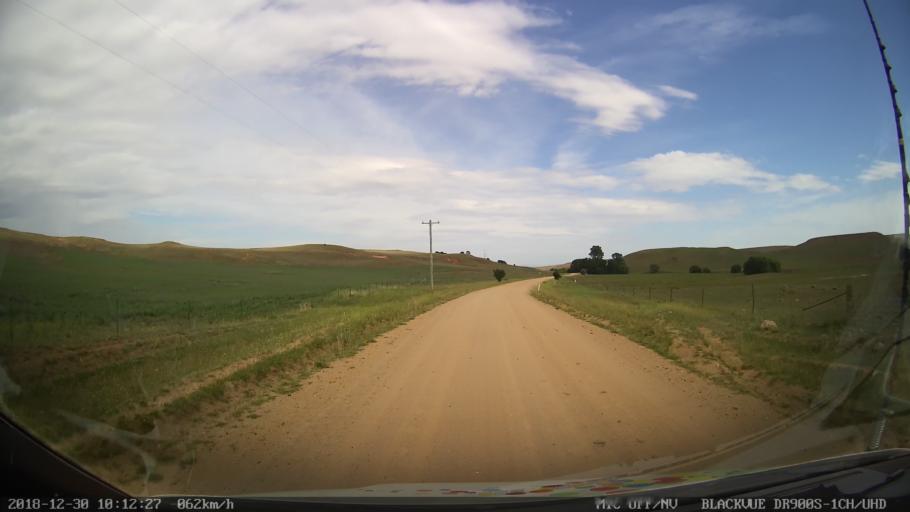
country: AU
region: New South Wales
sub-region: Snowy River
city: Berridale
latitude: -36.5417
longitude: 149.0760
